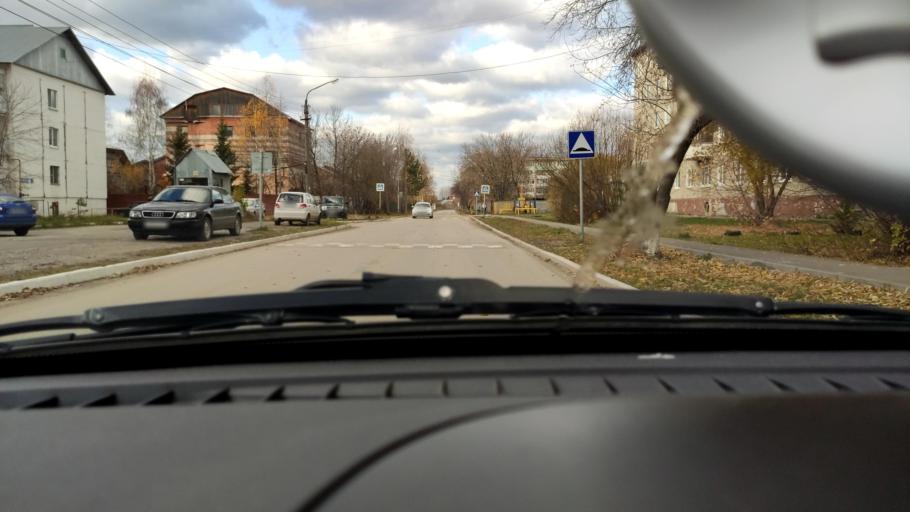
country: RU
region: Perm
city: Kondratovo
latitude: 57.9742
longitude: 56.1079
